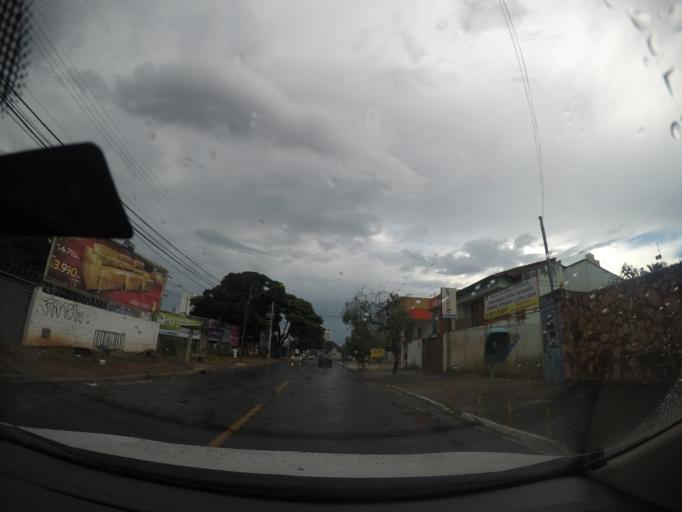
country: BR
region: Goias
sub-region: Goiania
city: Goiania
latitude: -16.7111
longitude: -49.2760
